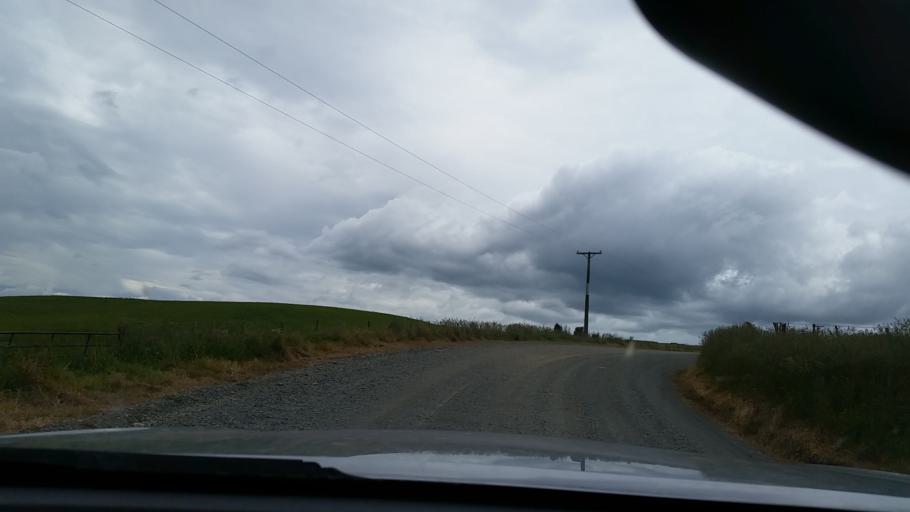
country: NZ
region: Southland
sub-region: Southland District
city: Winton
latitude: -45.8290
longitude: 168.1497
